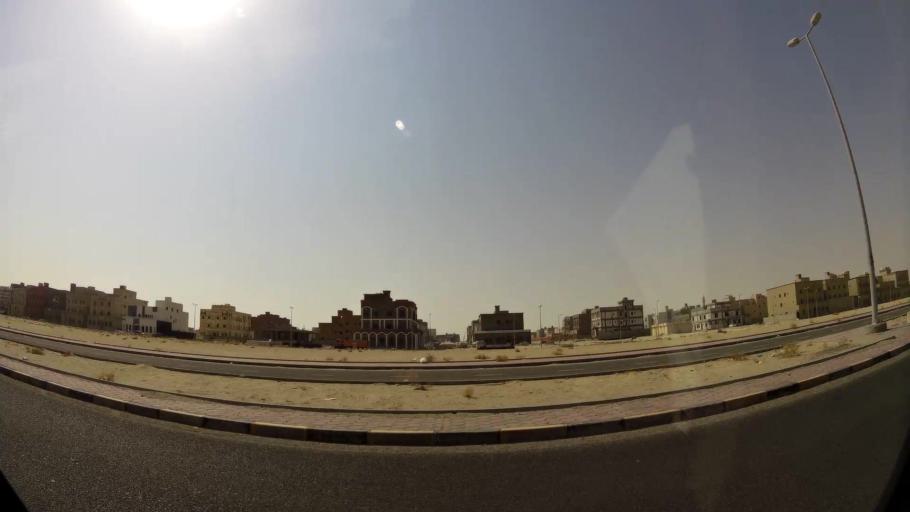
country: KW
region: Al Ahmadi
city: Al Wafrah
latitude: 28.7991
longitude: 48.0573
